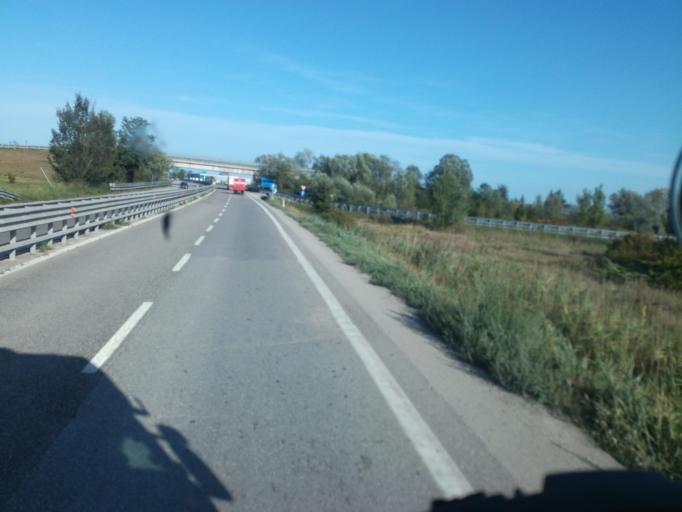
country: IT
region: Veneto
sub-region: Provincia di Rovigo
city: Villamarzana
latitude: 45.0197
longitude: 11.6998
